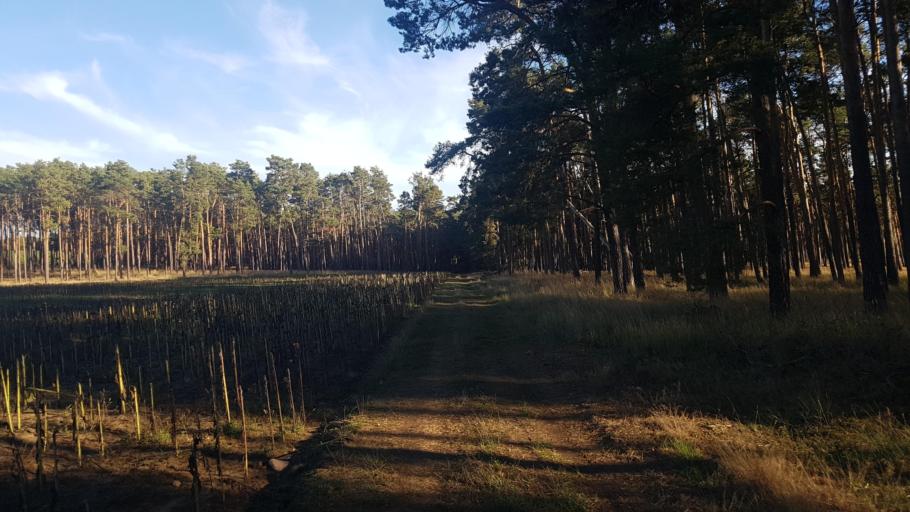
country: DE
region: Brandenburg
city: Herzberg
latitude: 51.6666
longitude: 13.3039
